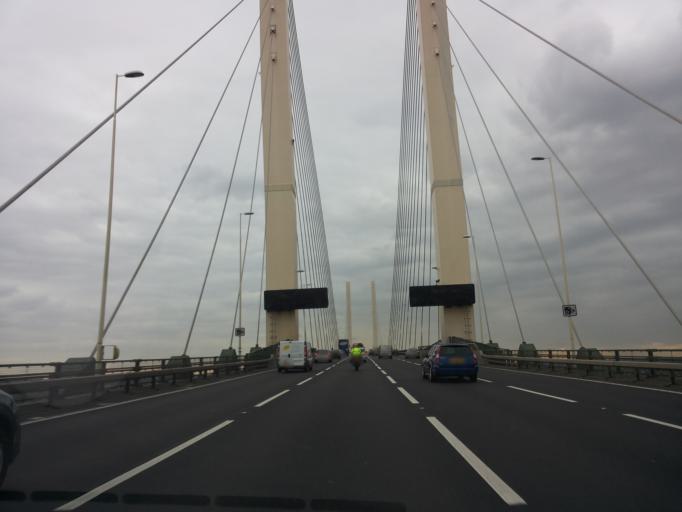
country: GB
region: England
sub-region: Kent
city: Stone
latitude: 51.4671
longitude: 0.2610
